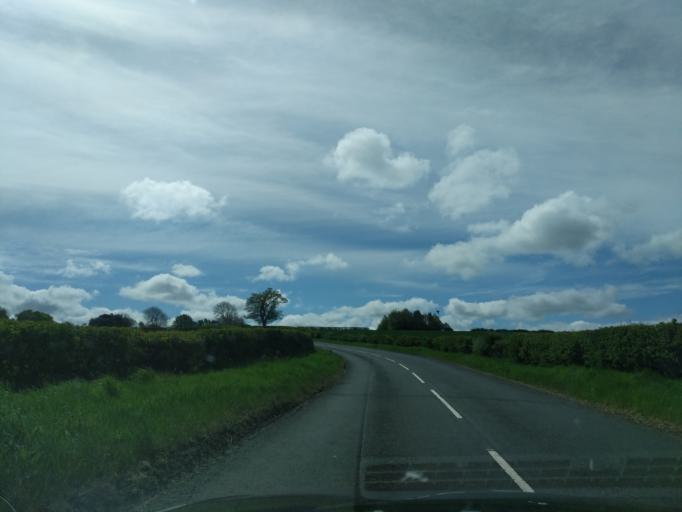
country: GB
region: Scotland
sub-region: The Scottish Borders
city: Saint Boswells
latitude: 55.6222
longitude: -2.5642
